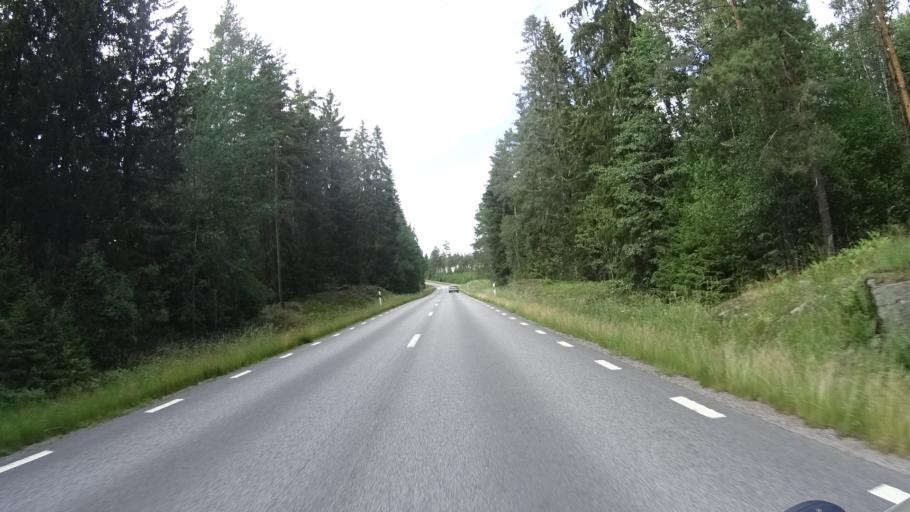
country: SE
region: OEstergoetland
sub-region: Atvidabergs Kommun
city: Atvidaberg
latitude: 58.1302
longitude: 16.0928
